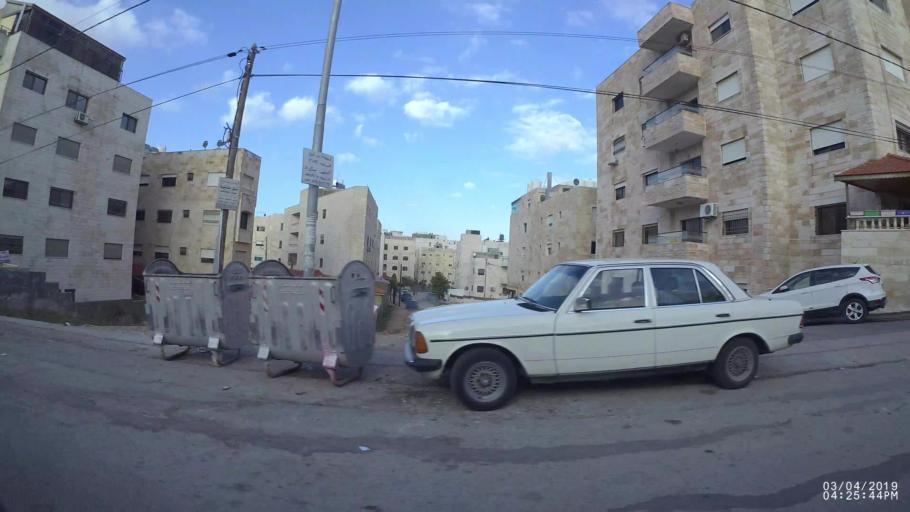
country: JO
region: Amman
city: Al Bunayyat ash Shamaliyah
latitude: 31.9118
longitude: 35.8900
